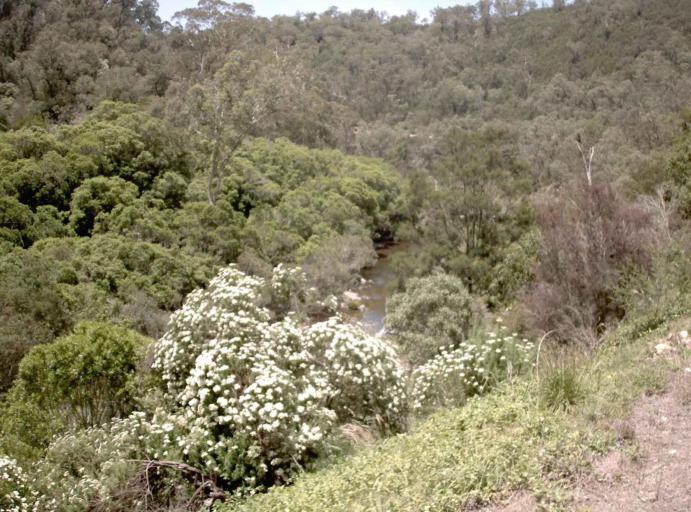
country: AU
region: Victoria
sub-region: East Gippsland
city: Lakes Entrance
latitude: -37.5328
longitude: 147.8537
